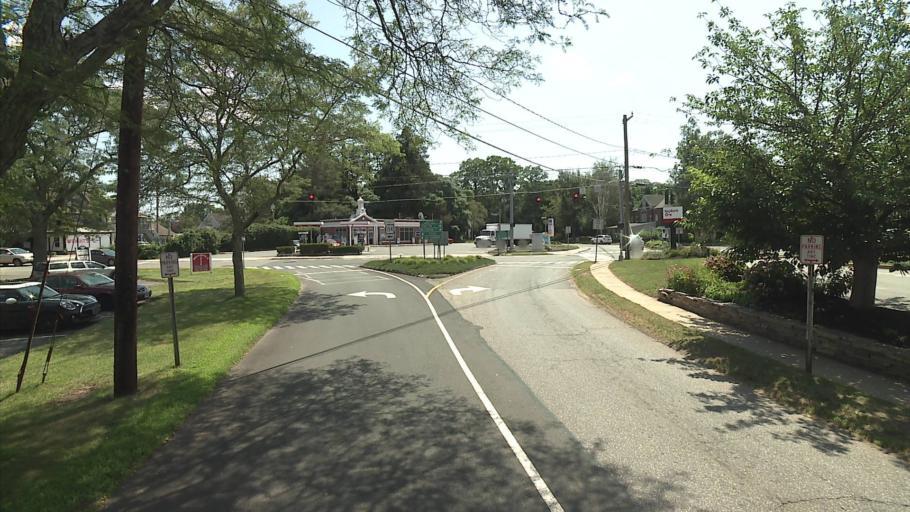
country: US
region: Connecticut
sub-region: Middlesex County
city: Essex Village
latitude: 41.3519
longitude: -72.4167
